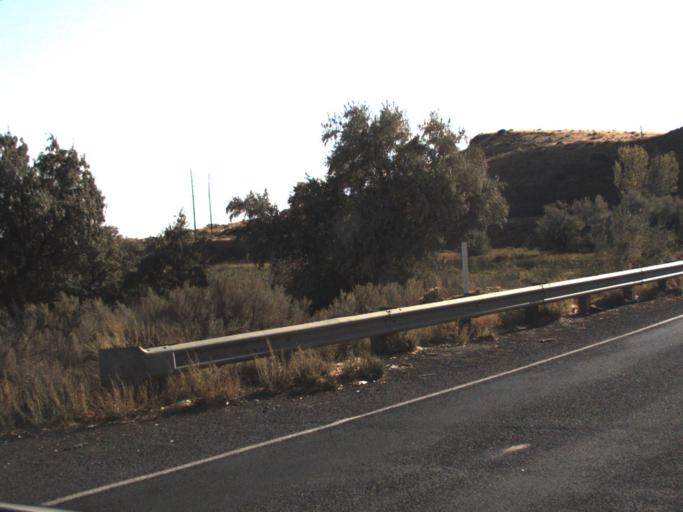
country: US
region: Oregon
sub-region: Morrow County
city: Boardman
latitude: 45.8946
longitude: -119.6929
